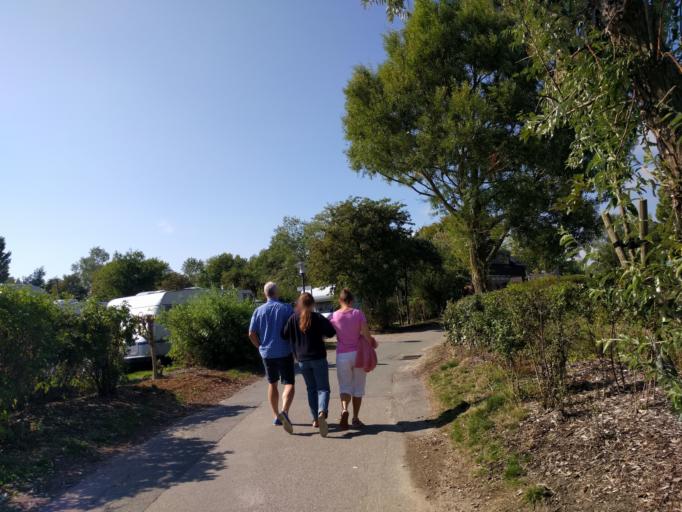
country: DE
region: Schleswig-Holstein
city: Burg auf Fehmarn
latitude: 54.4041
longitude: 11.1799
